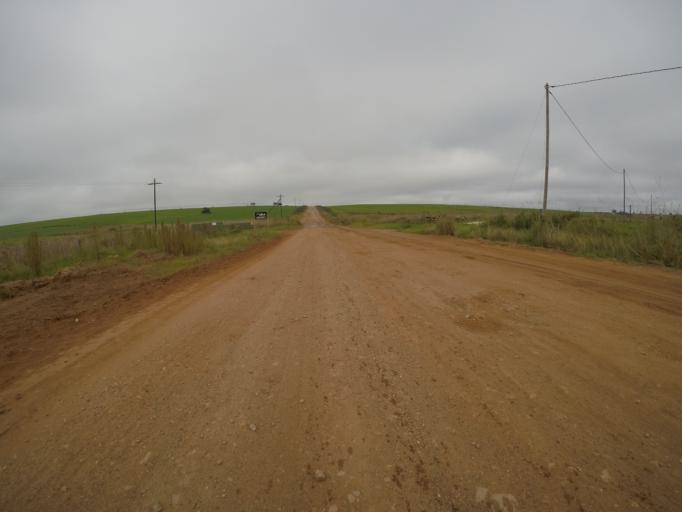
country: ZA
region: Eastern Cape
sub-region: Cacadu District Municipality
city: Kareedouw
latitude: -34.0183
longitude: 24.2391
